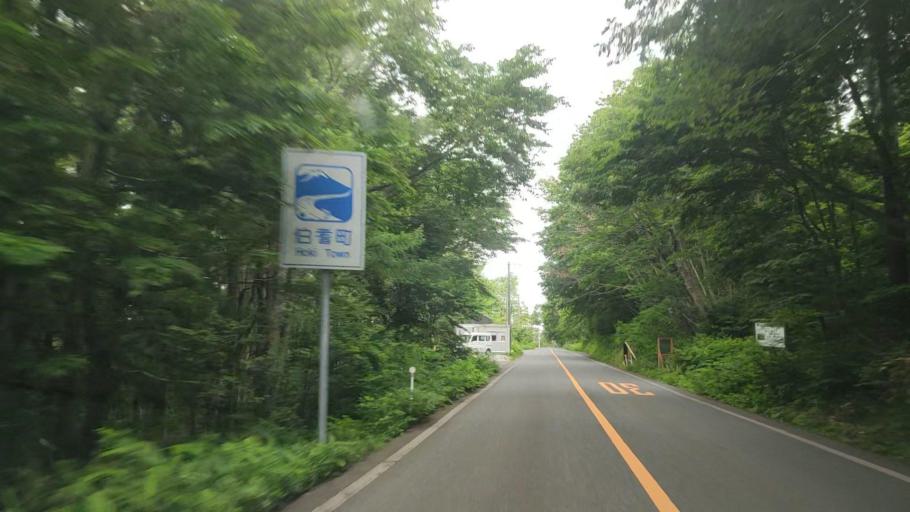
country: JP
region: Tottori
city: Yonago
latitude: 35.3598
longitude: 133.5276
